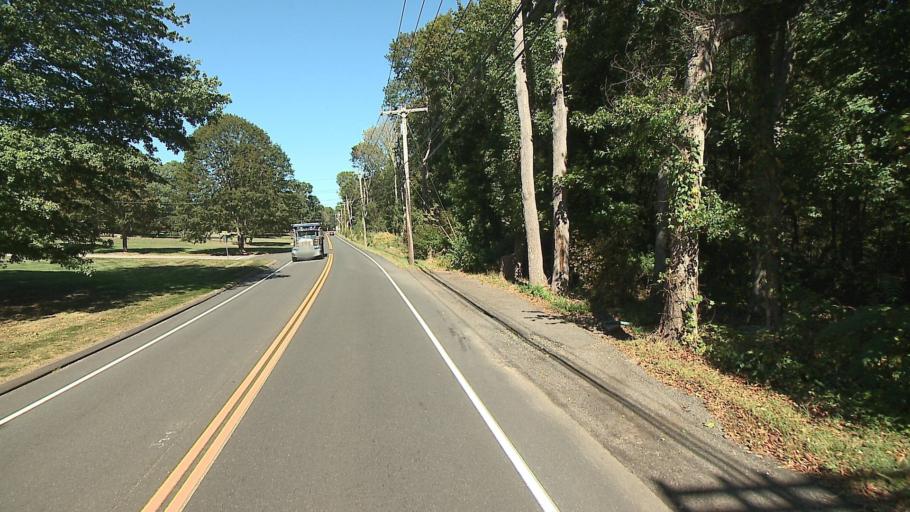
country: US
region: Connecticut
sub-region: New Haven County
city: Orange
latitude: 41.2990
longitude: -73.0256
